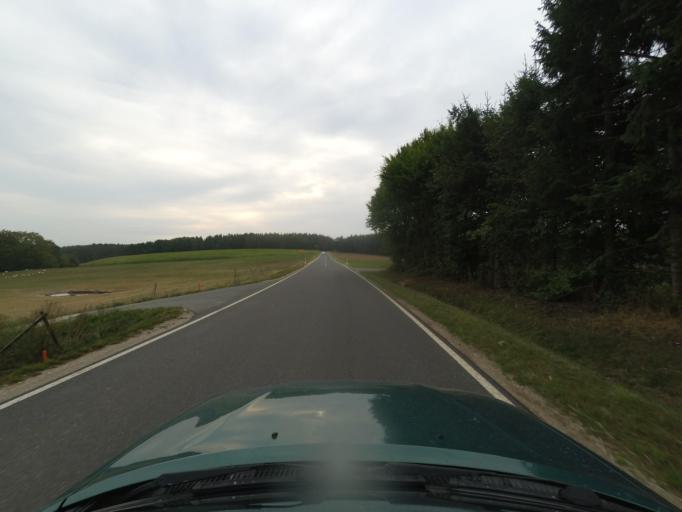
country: DE
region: Bavaria
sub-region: Upper Palatinate
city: Konigstein
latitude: 49.5790
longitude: 11.6560
